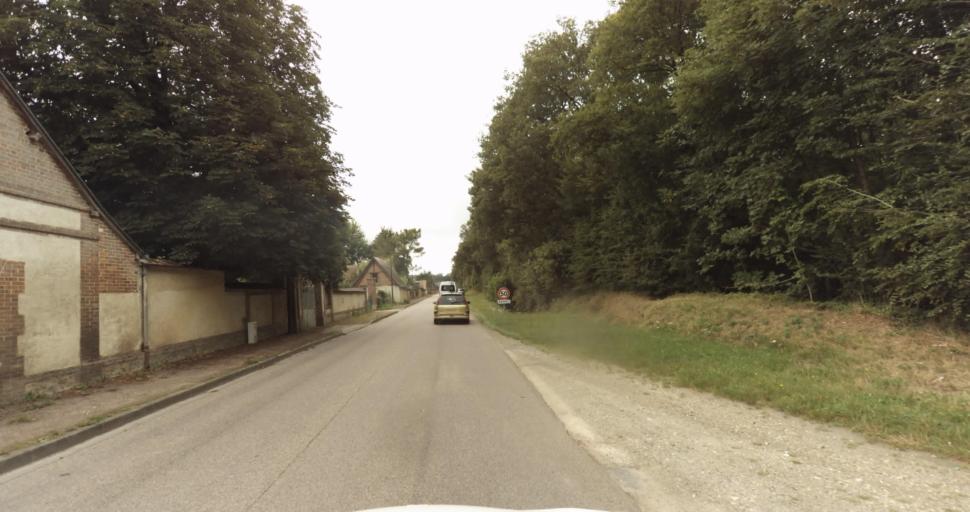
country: FR
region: Haute-Normandie
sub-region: Departement de l'Eure
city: Arnieres-sur-Iton
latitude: 48.9704
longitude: 1.0942
